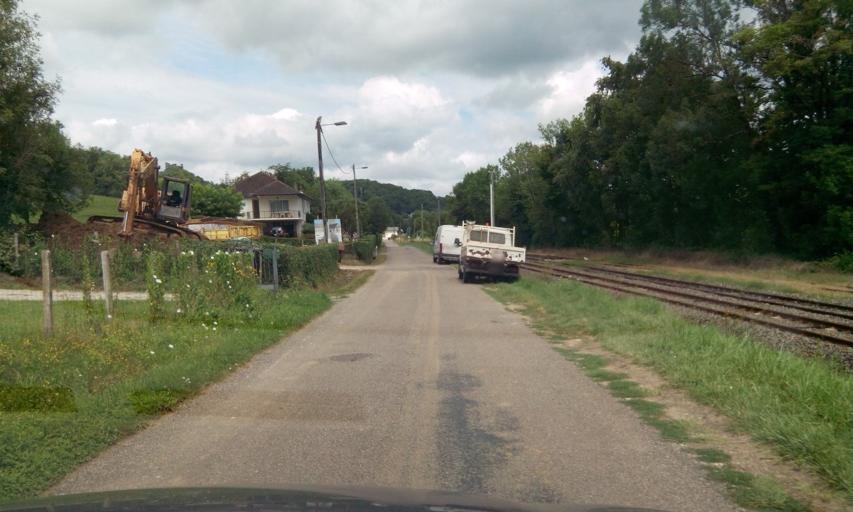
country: FR
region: Limousin
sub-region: Departement de la Correze
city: Meyssac
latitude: 45.0394
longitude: 1.5997
